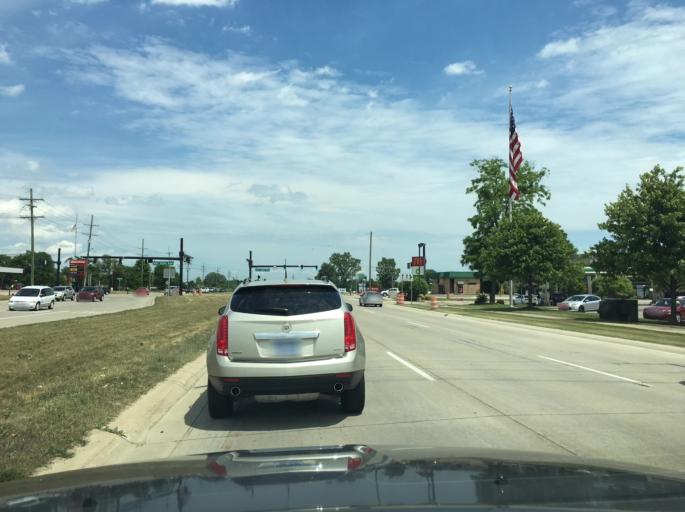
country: US
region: Michigan
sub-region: Macomb County
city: Shelby
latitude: 42.7136
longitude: -83.0367
